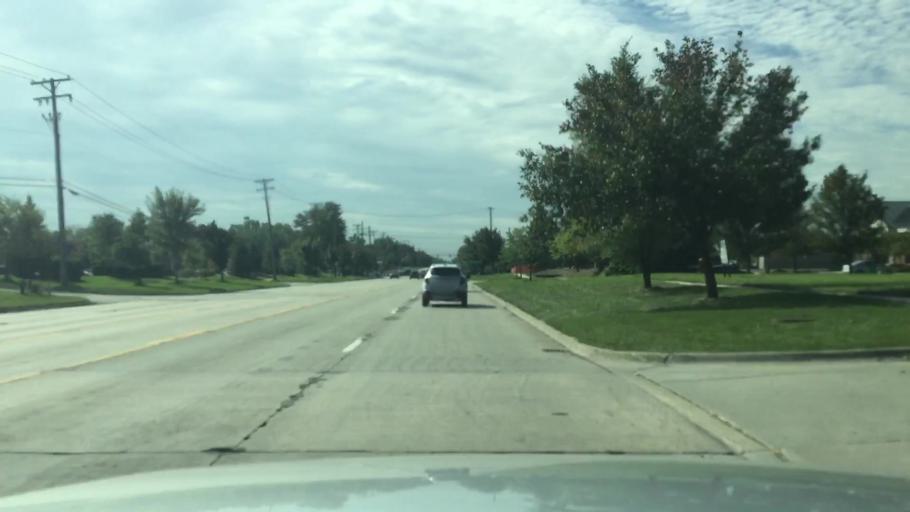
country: US
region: Michigan
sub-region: Wayne County
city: Canton
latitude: 42.3098
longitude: -83.4874
